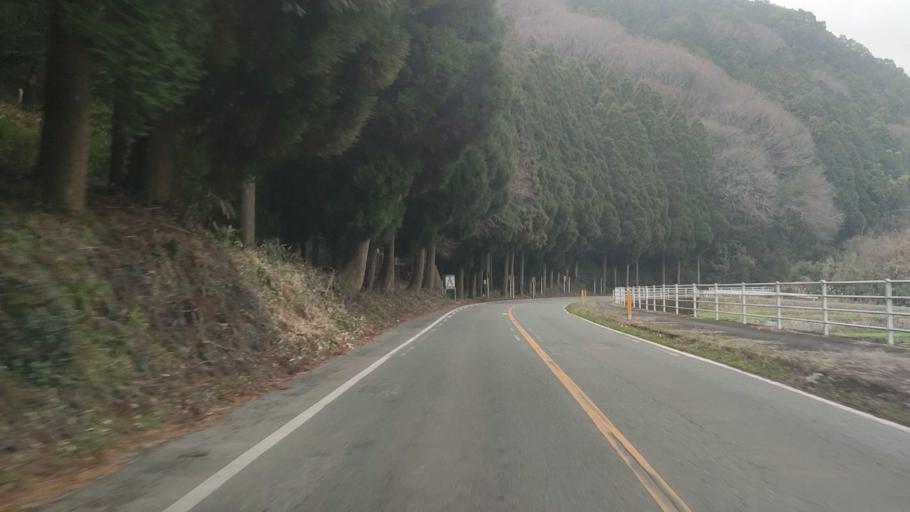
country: JP
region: Kumamoto
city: Ozu
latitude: 32.8521
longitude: 130.8689
